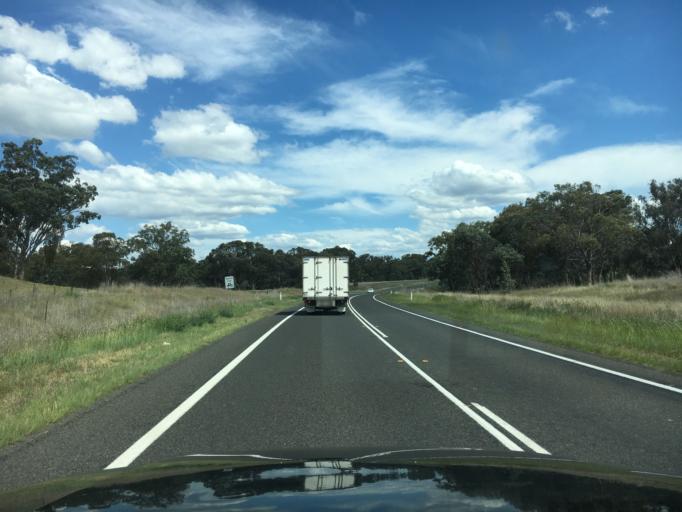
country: AU
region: New South Wales
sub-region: Liverpool Plains
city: Quirindi
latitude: -31.4825
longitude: 150.8635
